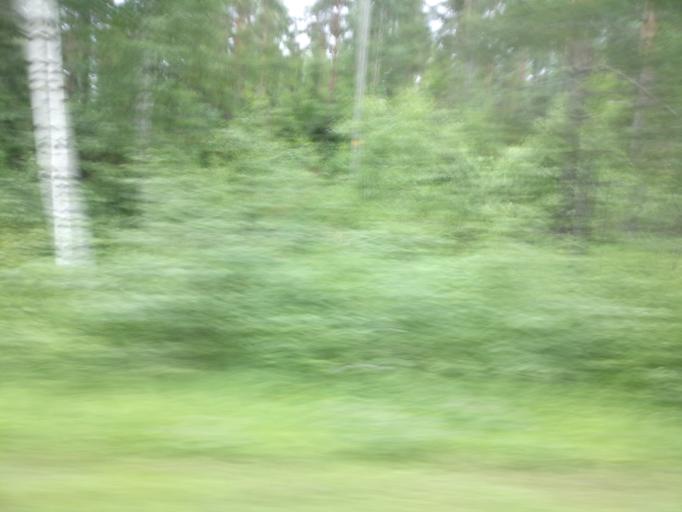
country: FI
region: Northern Savo
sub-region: Varkaus
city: Kangaslampi
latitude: 62.1654
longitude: 28.1340
